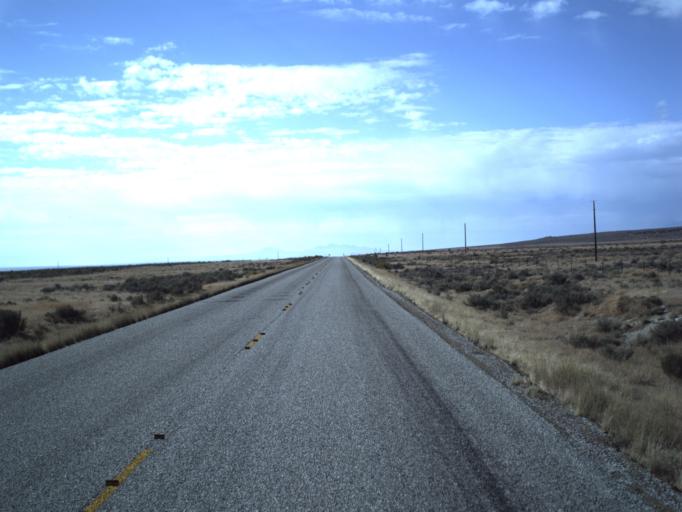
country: US
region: Utah
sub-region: Tooele County
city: Wendover
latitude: 41.5462
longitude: -113.5883
